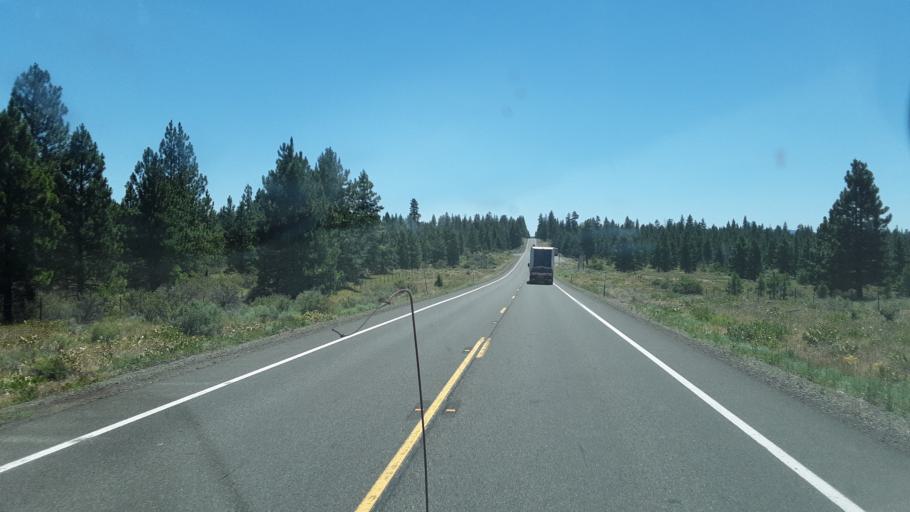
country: US
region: California
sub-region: Siskiyou County
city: Tulelake
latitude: 41.5762
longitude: -121.1855
